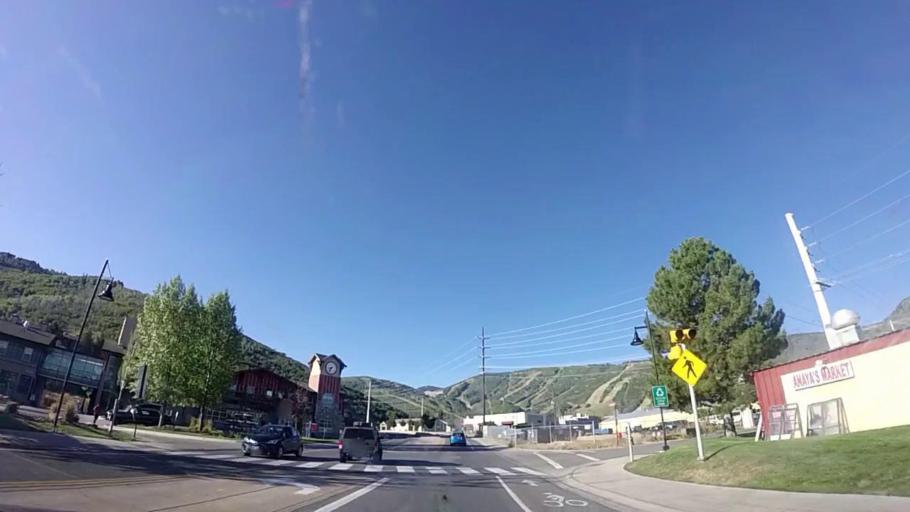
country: US
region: Utah
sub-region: Summit County
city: Park City
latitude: 40.6609
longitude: -111.5014
